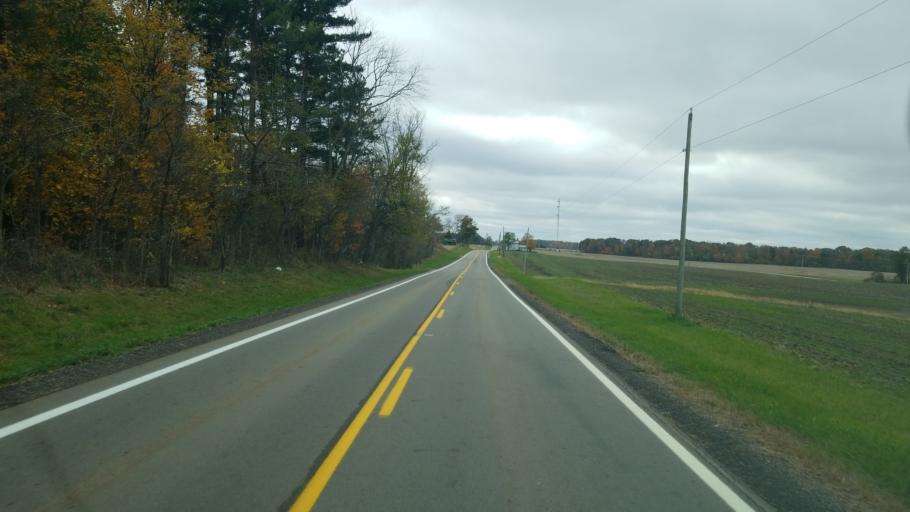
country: US
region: Ohio
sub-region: Richland County
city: Shelby
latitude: 40.9030
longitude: -82.7401
